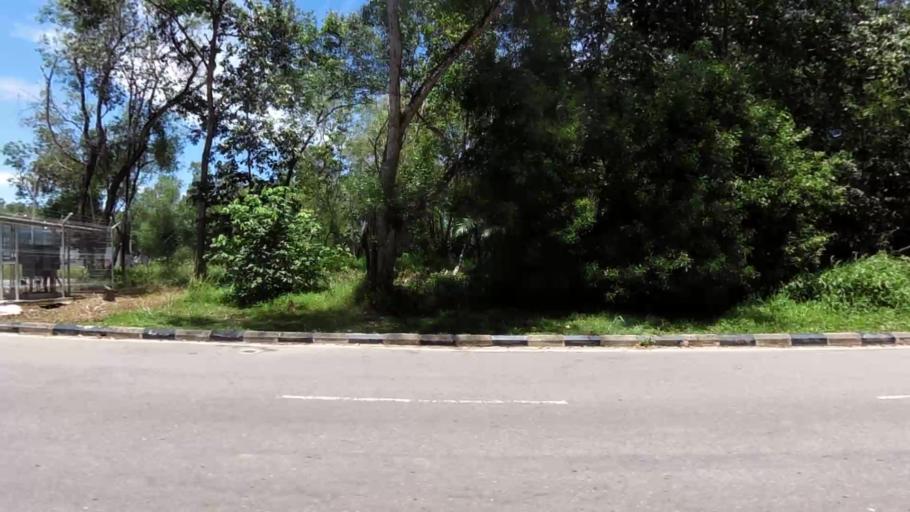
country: BN
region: Brunei and Muara
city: Bandar Seri Begawan
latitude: 4.9221
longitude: 114.9578
